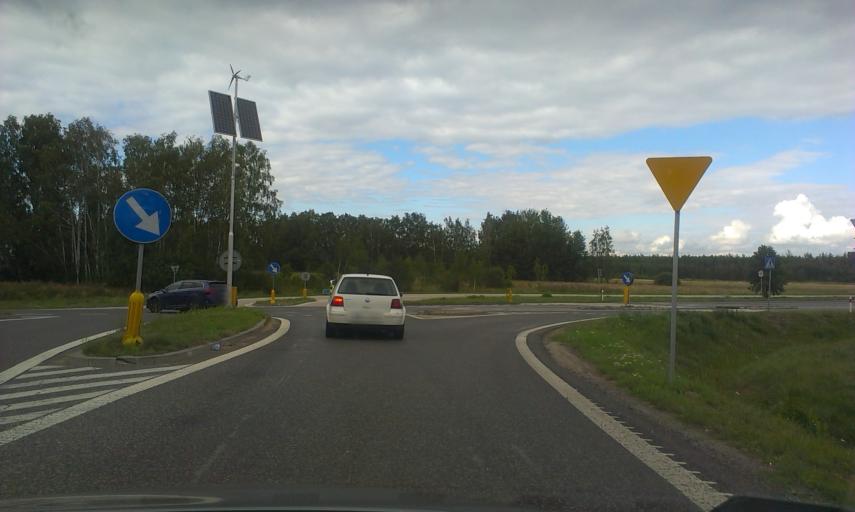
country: PL
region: Masovian Voivodeship
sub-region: Powiat zyrardowski
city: Mszczonow
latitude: 51.9931
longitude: 20.5026
